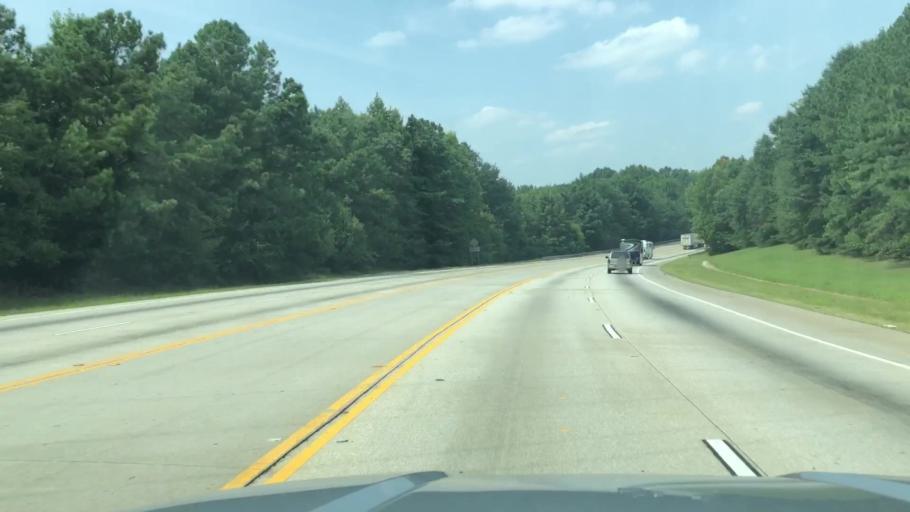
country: US
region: Georgia
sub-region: Douglas County
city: Lithia Springs
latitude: 33.8094
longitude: -84.6548
